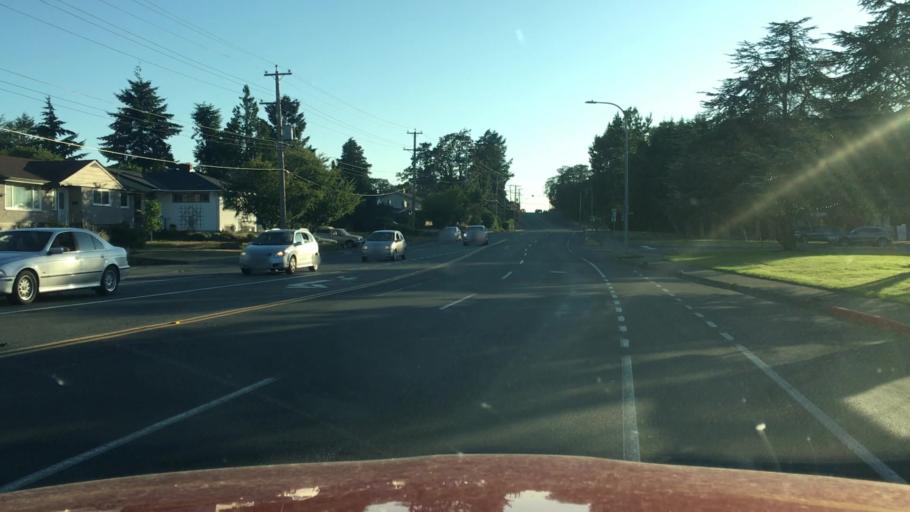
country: CA
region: British Columbia
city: Victoria
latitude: 48.4719
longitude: -123.3516
